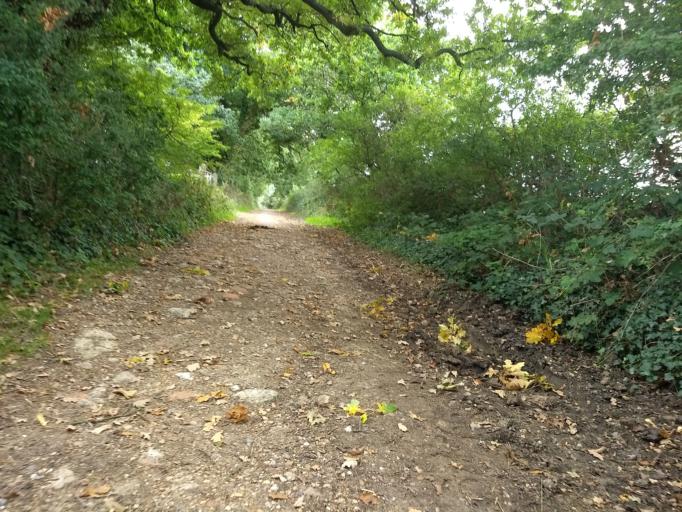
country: GB
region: England
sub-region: Isle of Wight
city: Newport
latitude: 50.7103
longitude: -1.2771
